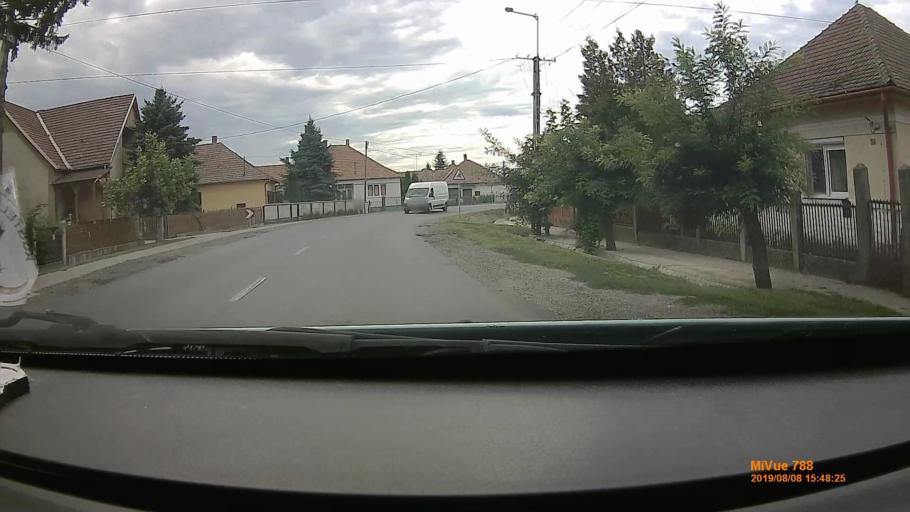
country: HU
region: Szabolcs-Szatmar-Bereg
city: Kocsord
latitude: 47.9388
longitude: 22.3771
